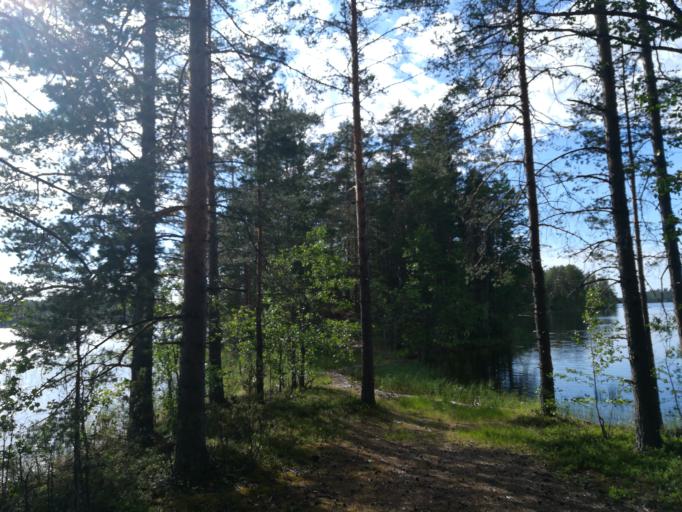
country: FI
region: Southern Savonia
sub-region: Savonlinna
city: Savonlinna
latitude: 61.6431
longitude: 28.7116
